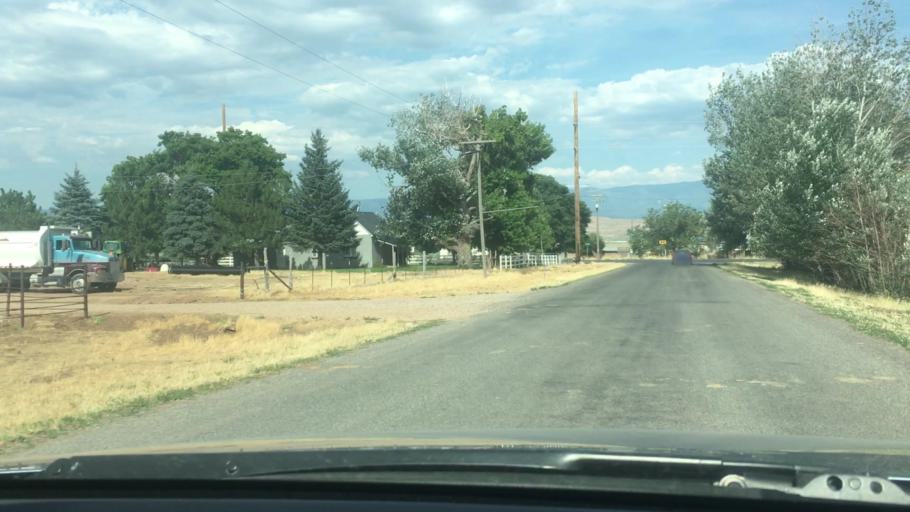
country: US
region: Utah
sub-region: Sanpete County
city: Moroni
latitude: 39.5421
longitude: -111.6414
